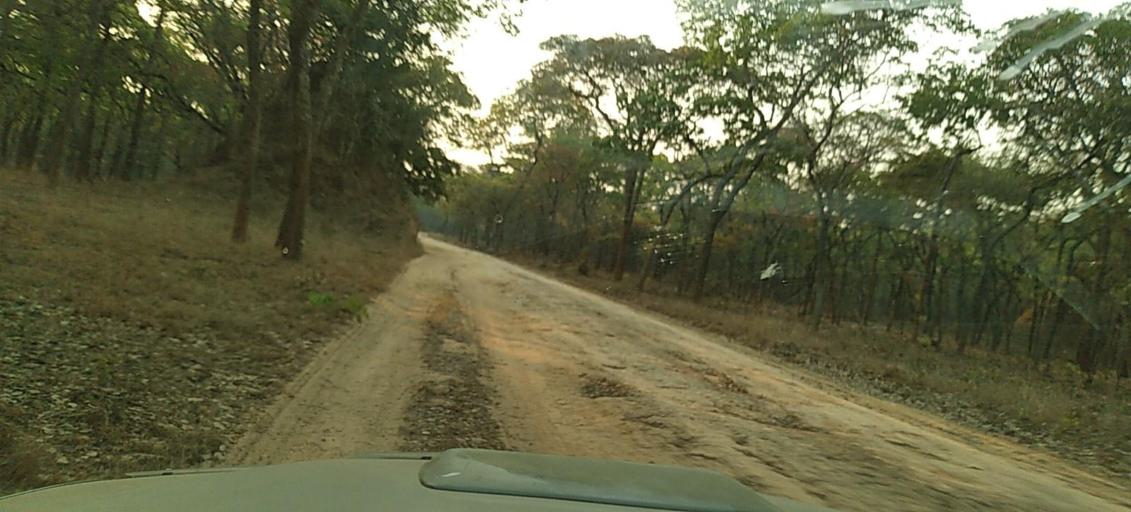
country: ZM
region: North-Western
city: Kasempa
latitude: -13.1562
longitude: 26.4456
